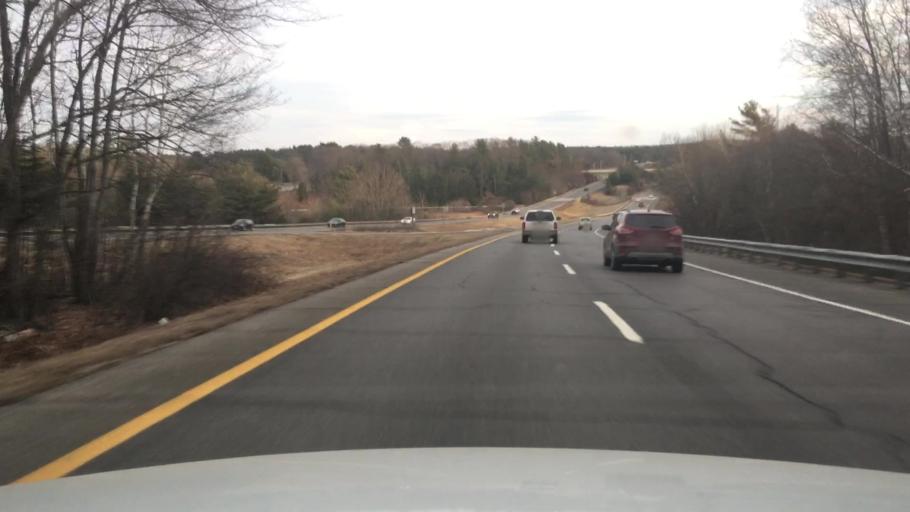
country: US
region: Maine
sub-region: Sagadahoc County
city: Bath
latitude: 43.9189
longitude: -69.8698
